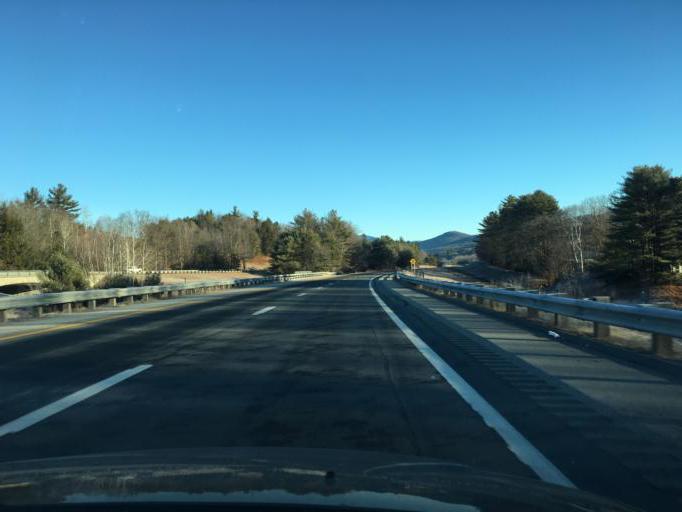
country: US
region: New Hampshire
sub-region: Grafton County
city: Plymouth
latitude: 43.8106
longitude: -71.6708
